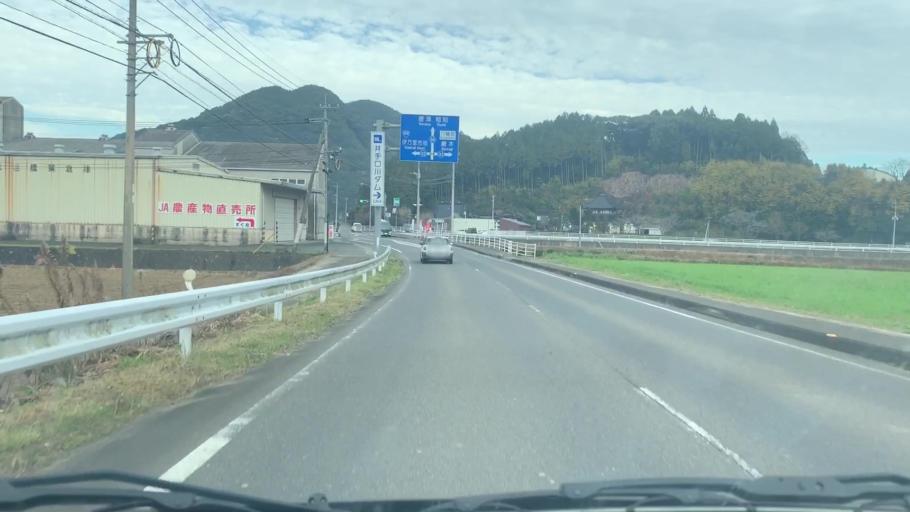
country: JP
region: Saga Prefecture
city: Imaricho-ko
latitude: 33.3002
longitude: 129.9696
